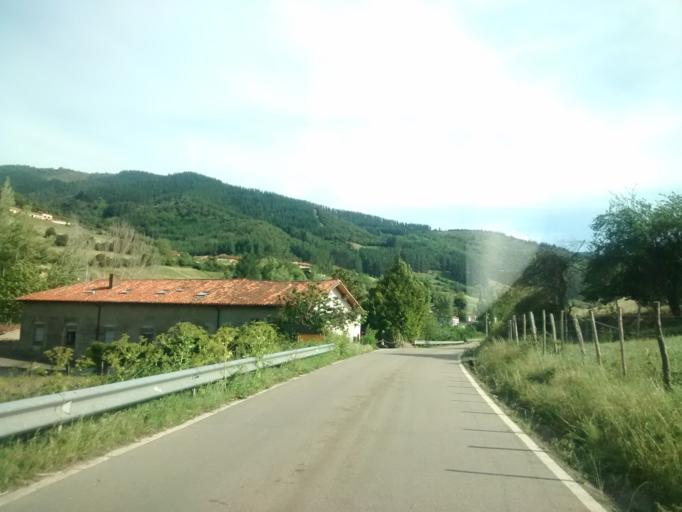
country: ES
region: Cantabria
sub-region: Provincia de Cantabria
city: Potes
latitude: 43.1773
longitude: -4.6022
